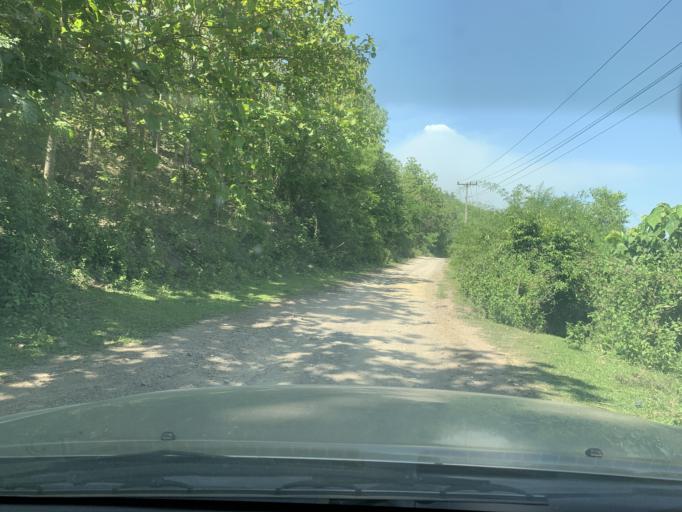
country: LA
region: Louangphabang
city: Louangphabang
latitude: 19.9110
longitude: 102.2598
